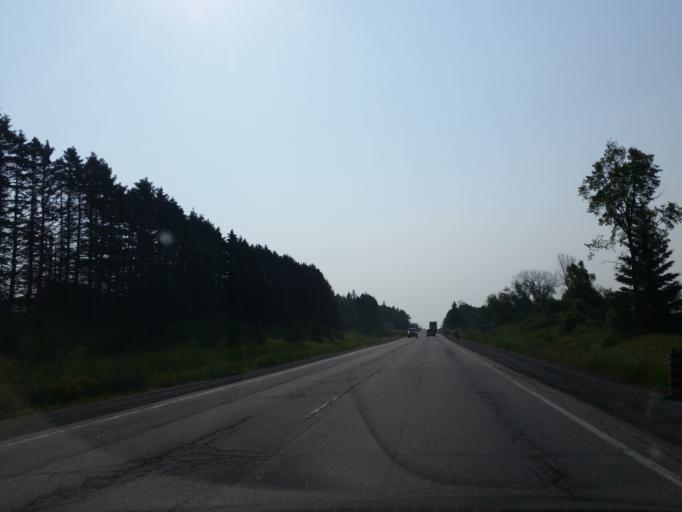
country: CA
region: Ontario
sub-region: Nipissing District
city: North Bay
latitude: 46.4201
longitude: -80.1609
